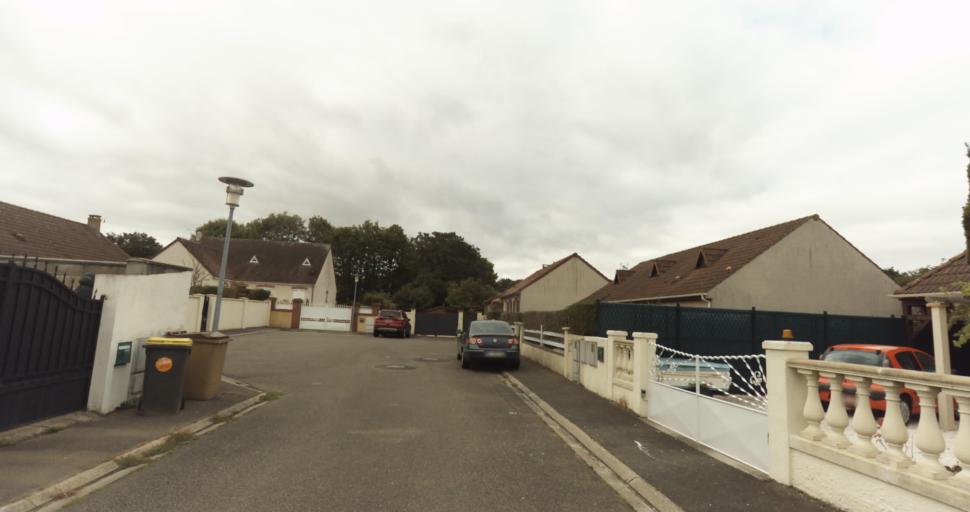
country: FR
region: Centre
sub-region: Departement d'Eure-et-Loir
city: Vernouillet
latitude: 48.7150
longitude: 1.3596
